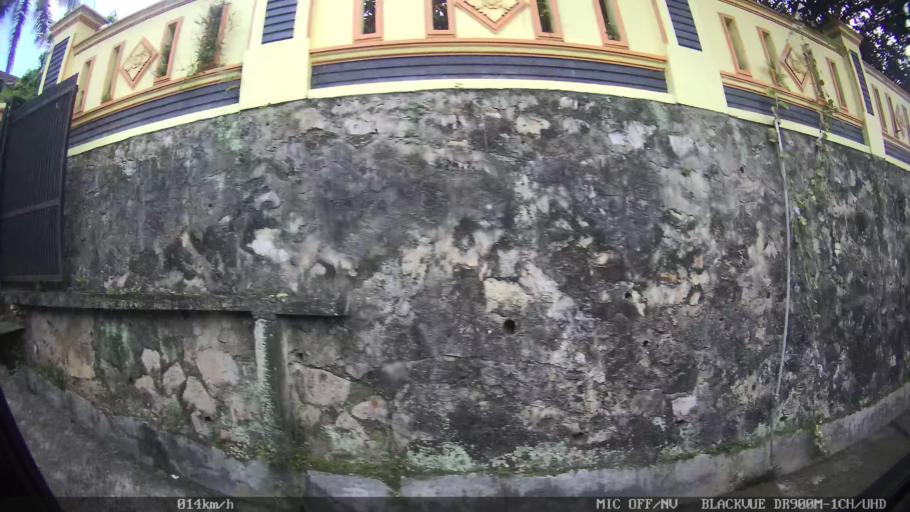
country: ID
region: Lampung
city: Kedaton
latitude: -5.3982
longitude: 105.2176
